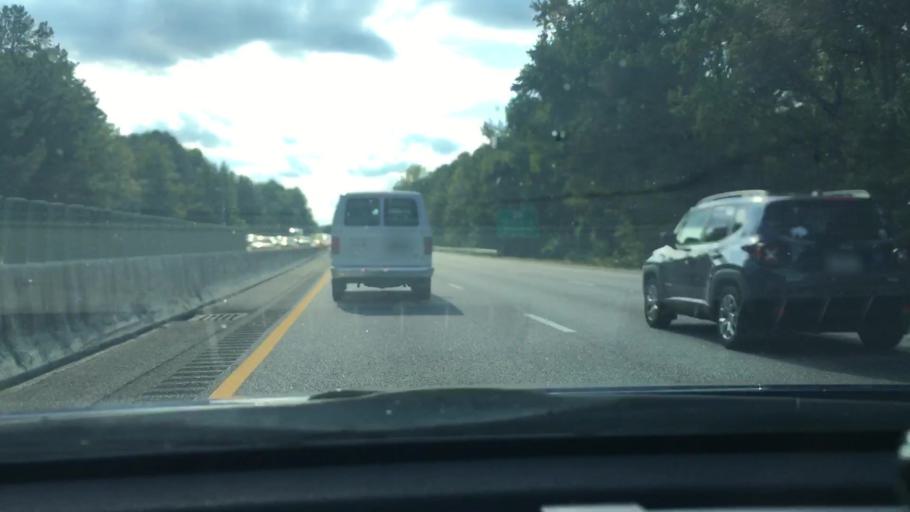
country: US
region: South Carolina
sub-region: Richland County
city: Dentsville
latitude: 34.0722
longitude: -81.0107
